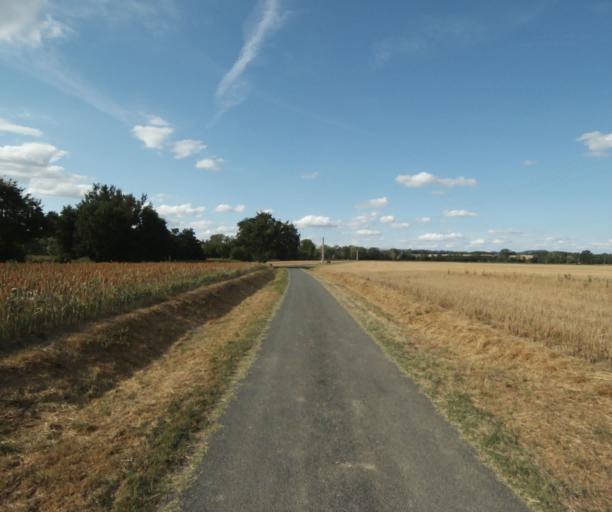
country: FR
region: Midi-Pyrenees
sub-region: Departement de la Haute-Garonne
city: Revel
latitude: 43.5161
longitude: 1.9906
